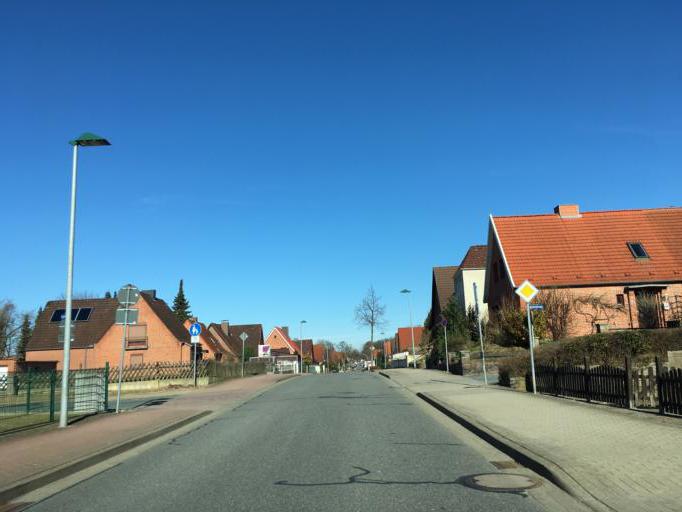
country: DE
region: Schleswig-Holstein
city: Molln
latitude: 53.6190
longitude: 10.6940
